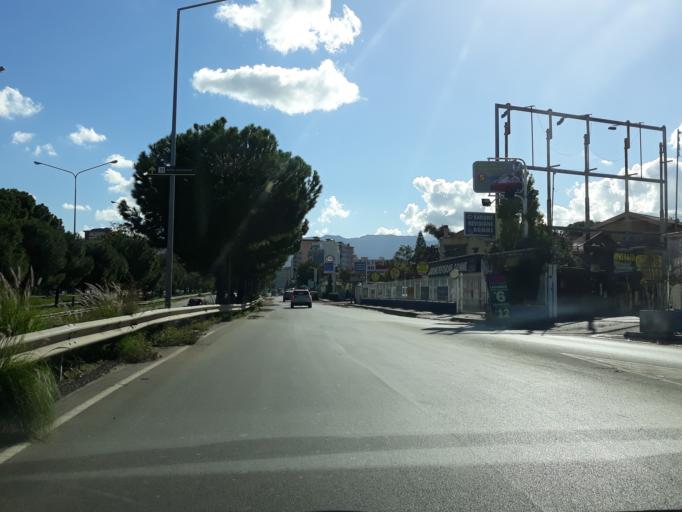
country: IT
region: Sicily
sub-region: Palermo
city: Palermo
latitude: 38.1384
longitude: 13.3308
